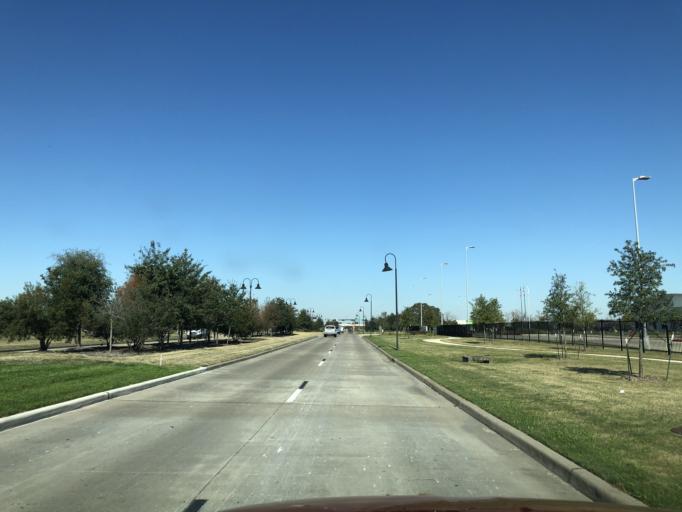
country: US
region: Texas
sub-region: Fort Bend County
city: Fresno
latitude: 29.5896
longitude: -95.4005
